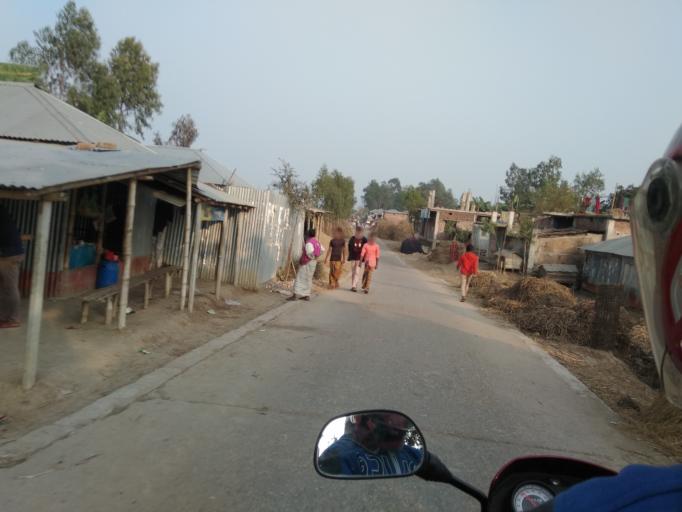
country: BD
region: Rajshahi
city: Ishurdi
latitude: 24.4808
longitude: 89.2335
